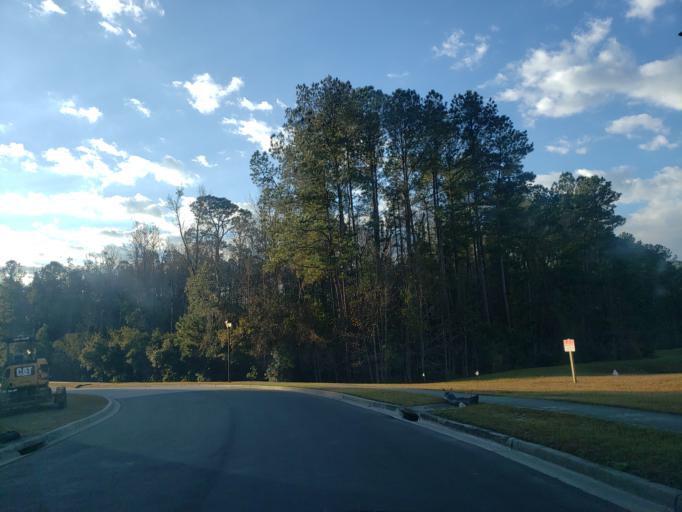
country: US
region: Georgia
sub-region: Chatham County
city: Bloomingdale
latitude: 32.1571
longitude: -81.2658
